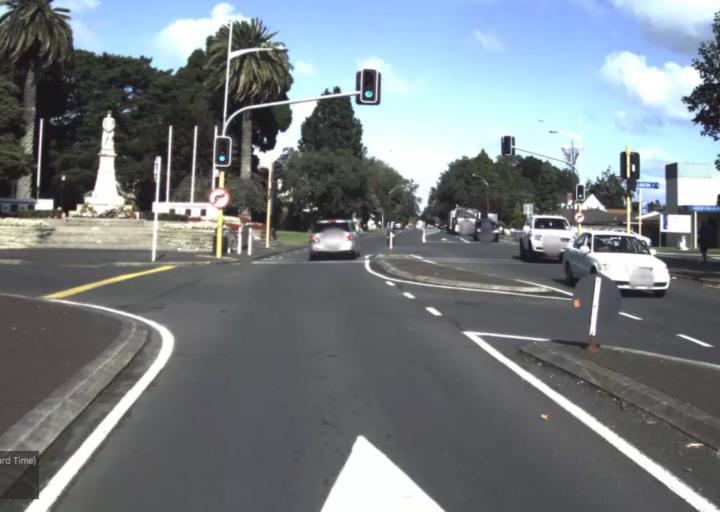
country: NZ
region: Auckland
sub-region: Auckland
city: Papakura
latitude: -37.0661
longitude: 174.9439
